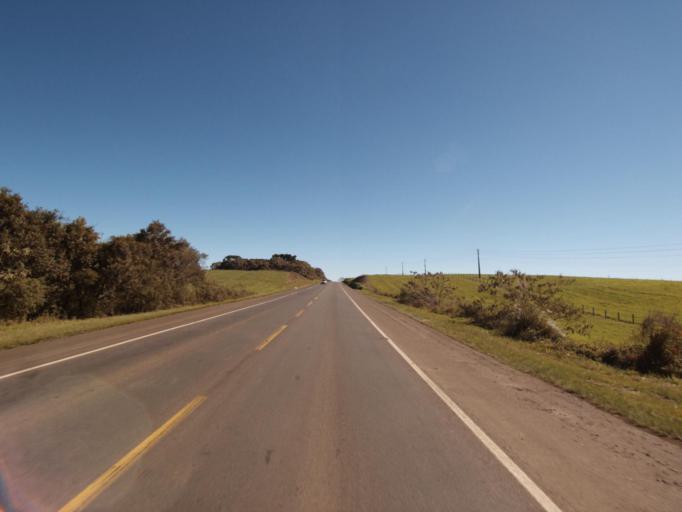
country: BR
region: Santa Catarina
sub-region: Xanxere
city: Xanxere
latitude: -26.8645
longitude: -52.2155
